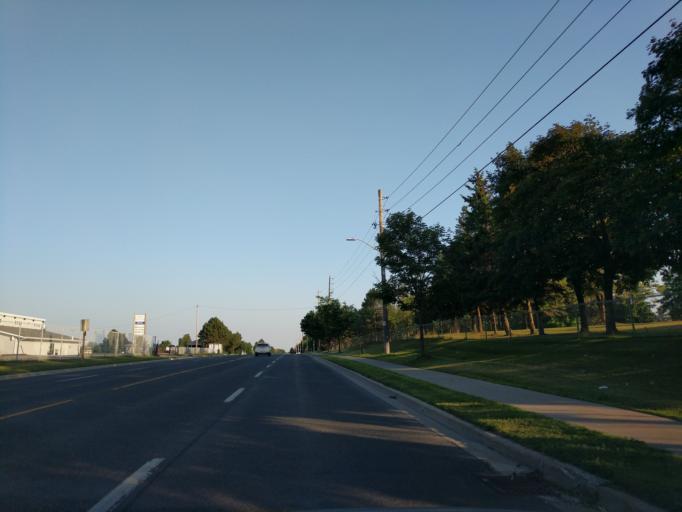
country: CA
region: Ontario
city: Oshawa
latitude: 43.9208
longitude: -78.9059
